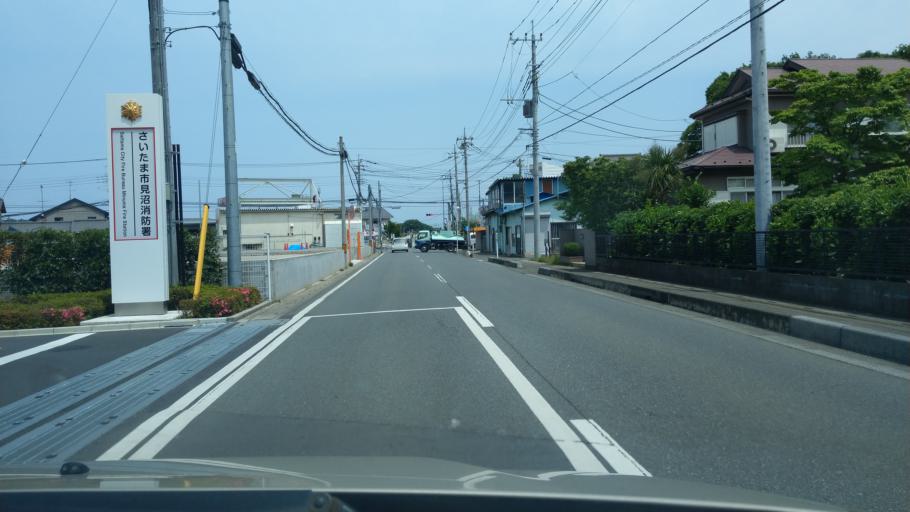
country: JP
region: Saitama
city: Saitama
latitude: 35.9042
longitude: 139.6878
